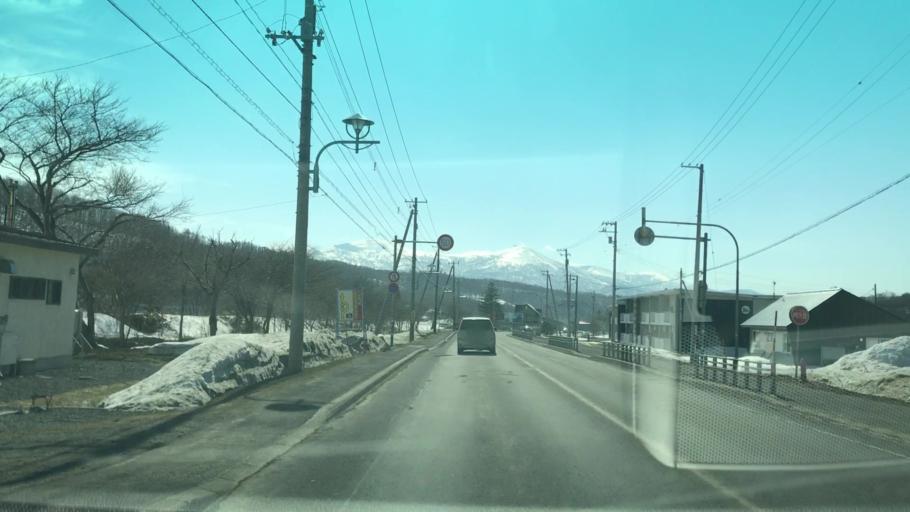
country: JP
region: Hokkaido
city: Iwanai
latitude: 42.9804
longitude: 140.6469
